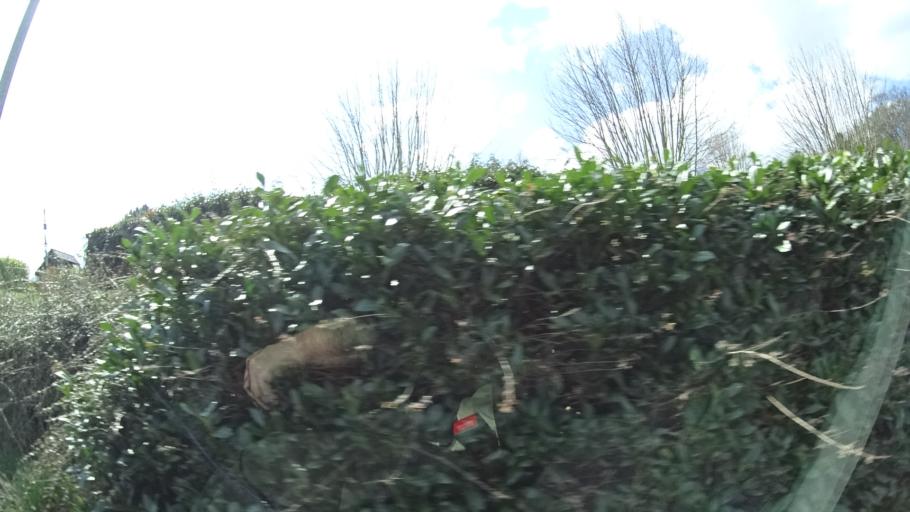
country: DE
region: Rheinland-Pfalz
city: Kirschweiler
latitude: 49.7586
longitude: 7.2401
